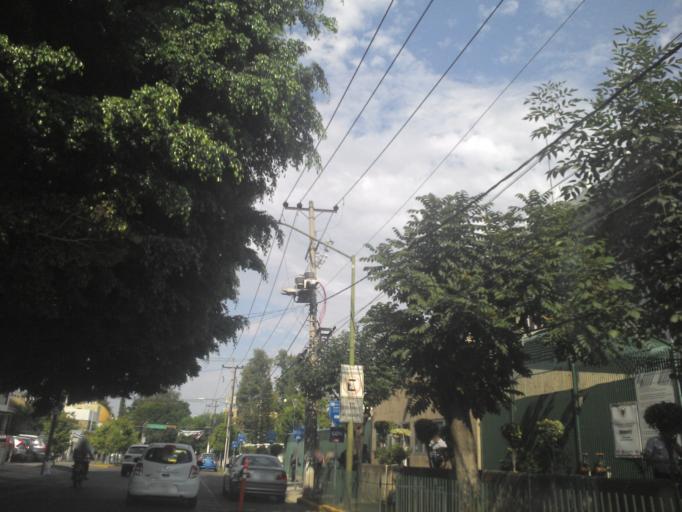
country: MX
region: Jalisco
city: Guadalajara
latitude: 20.6738
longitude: -103.3671
